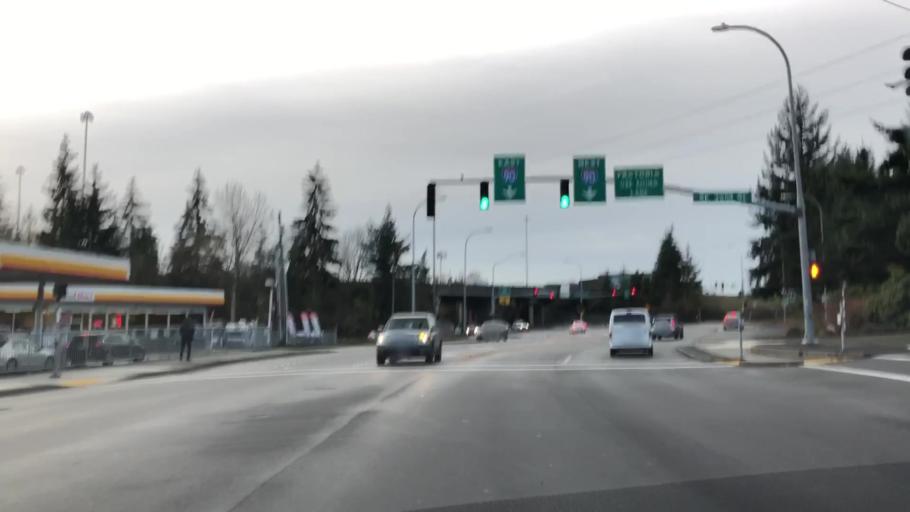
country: US
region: Washington
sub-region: King County
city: Newport
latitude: 47.5820
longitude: -122.1678
